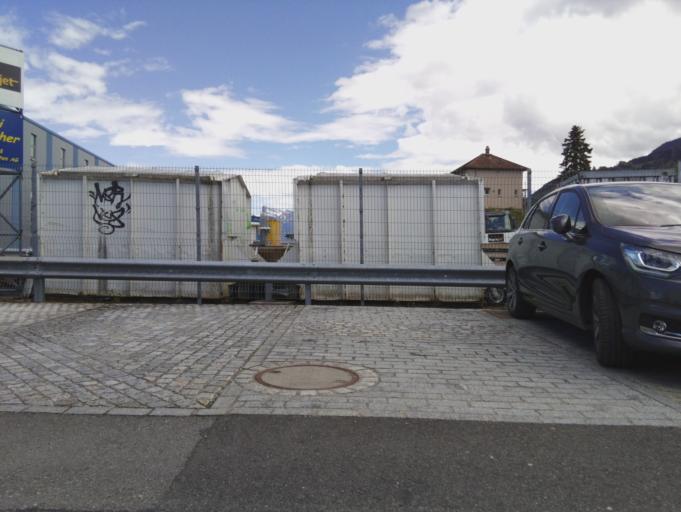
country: CH
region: Schwyz
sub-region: Bezirk March
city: Schubelbach
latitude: 47.1751
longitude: 8.9108
